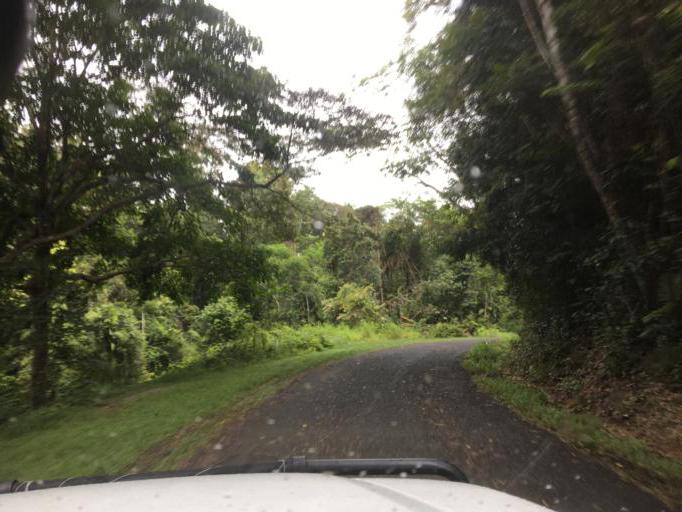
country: AU
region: Queensland
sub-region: Tablelands
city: Kuranda
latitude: -16.8453
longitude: 145.6428
